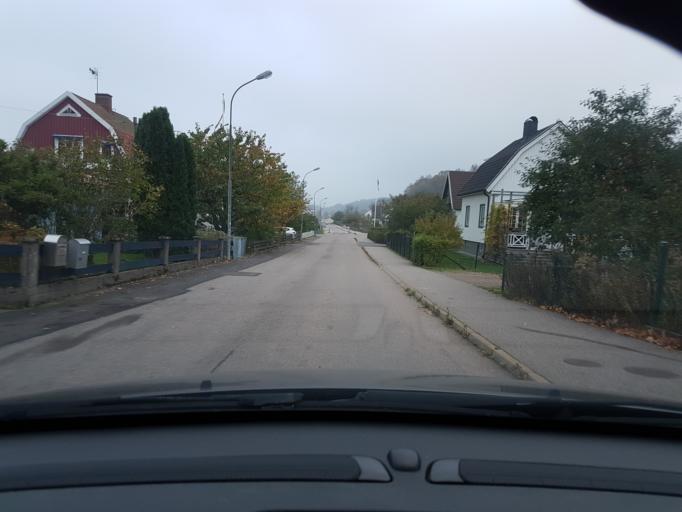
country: SE
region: Vaestra Goetaland
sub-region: Ale Kommun
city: Surte
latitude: 57.8241
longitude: 12.0213
